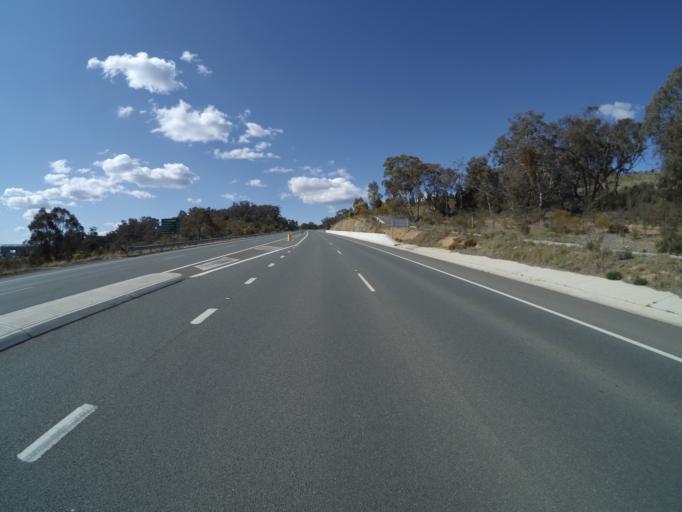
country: AU
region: New South Wales
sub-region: Queanbeyan
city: Queanbeyan
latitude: -35.3439
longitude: 149.2510
